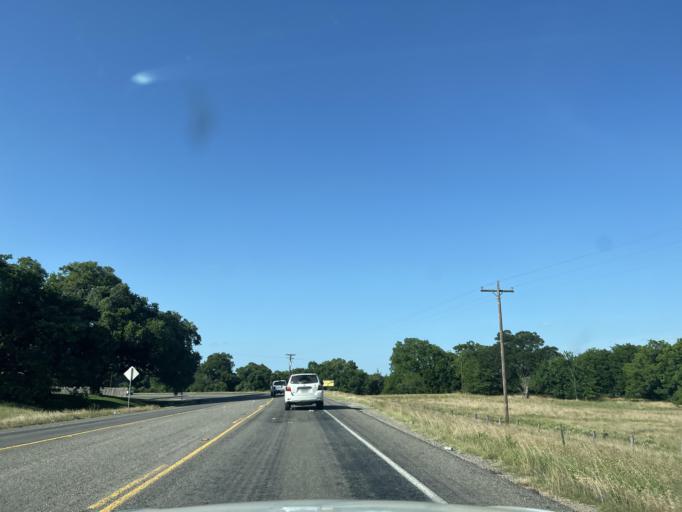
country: US
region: Texas
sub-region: Washington County
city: Brenham
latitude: 30.1447
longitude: -96.3625
